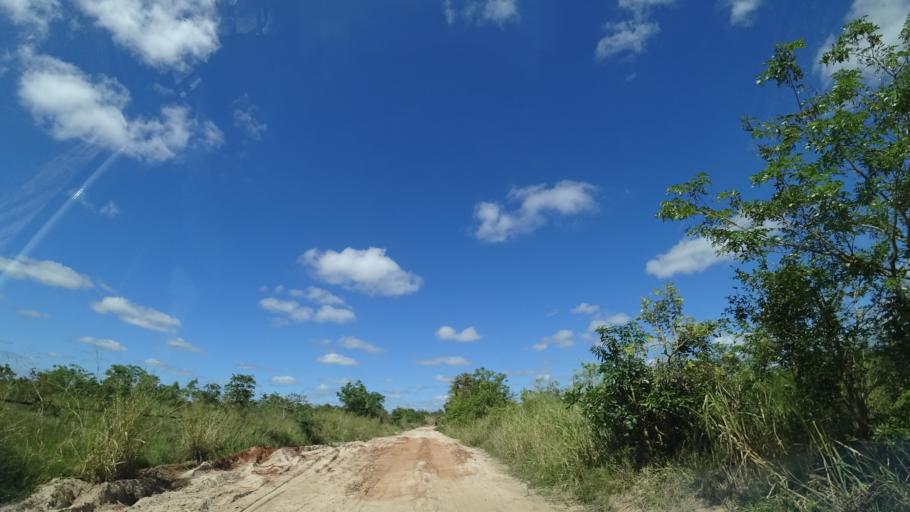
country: MZ
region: Sofala
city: Dondo
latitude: -19.2998
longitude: 34.6911
